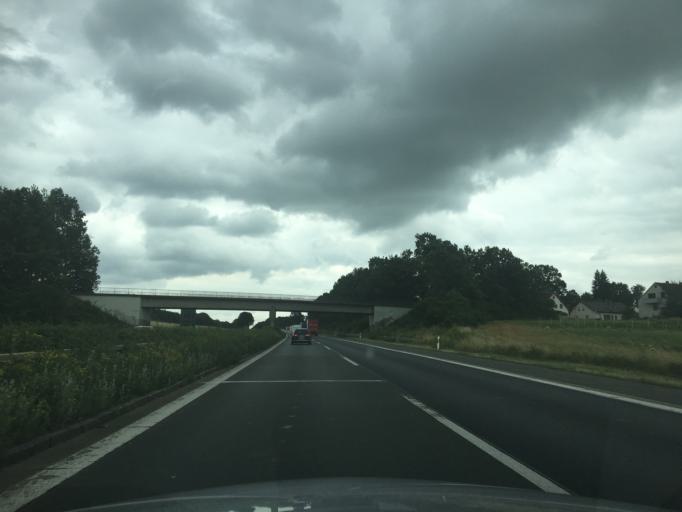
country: DE
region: Bavaria
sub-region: Regierungsbezirk Mittelfranken
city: Gremsdorf
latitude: 49.6852
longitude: 10.8627
